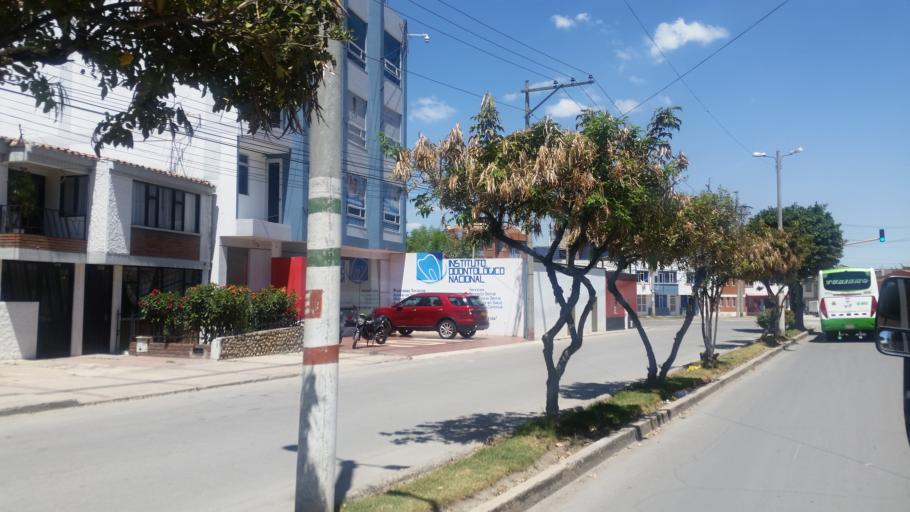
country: CO
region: Boyaca
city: Sogamoso
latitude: 5.7233
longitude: -72.9266
